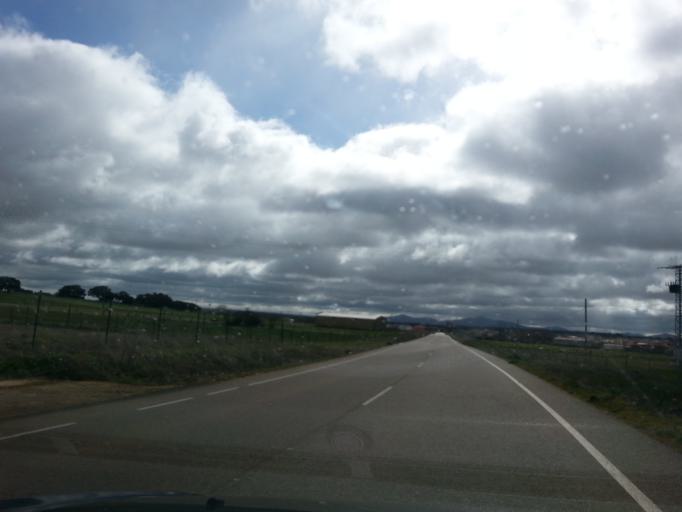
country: ES
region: Castille and Leon
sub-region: Provincia de Salamanca
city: Cabrillas
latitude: 40.7475
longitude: -6.1830
